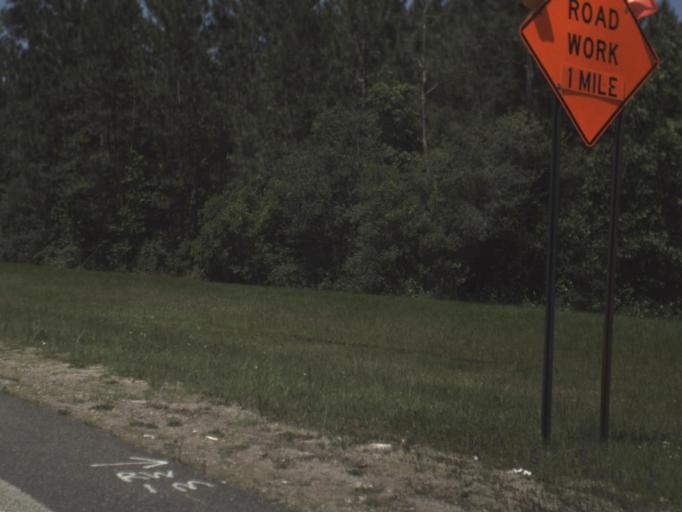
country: US
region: Florida
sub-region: Clay County
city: Bellair-Meadowbrook Terrace
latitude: 30.1970
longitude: -81.8375
